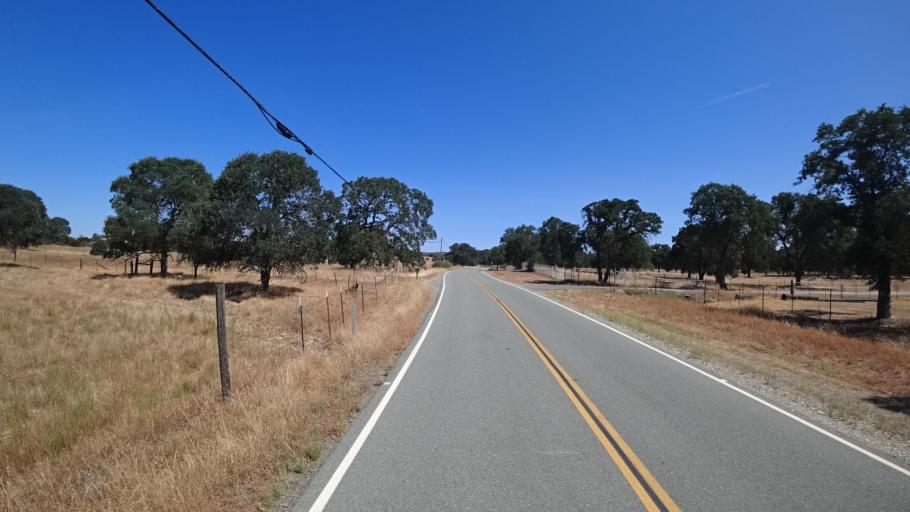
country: US
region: California
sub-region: Calaveras County
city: Rancho Calaveras
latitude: 38.1782
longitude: -120.9088
